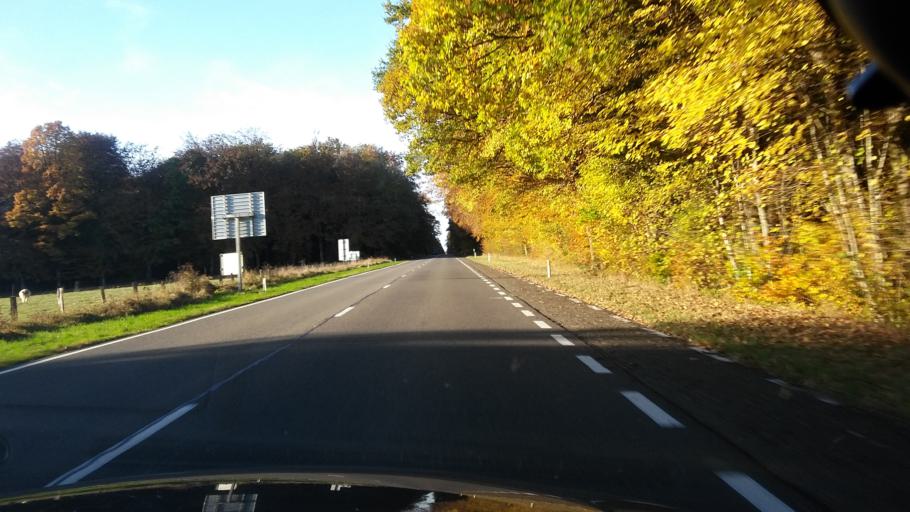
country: BE
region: Wallonia
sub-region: Province du Luxembourg
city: Herbeumont
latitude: 49.7368
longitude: 5.2259
